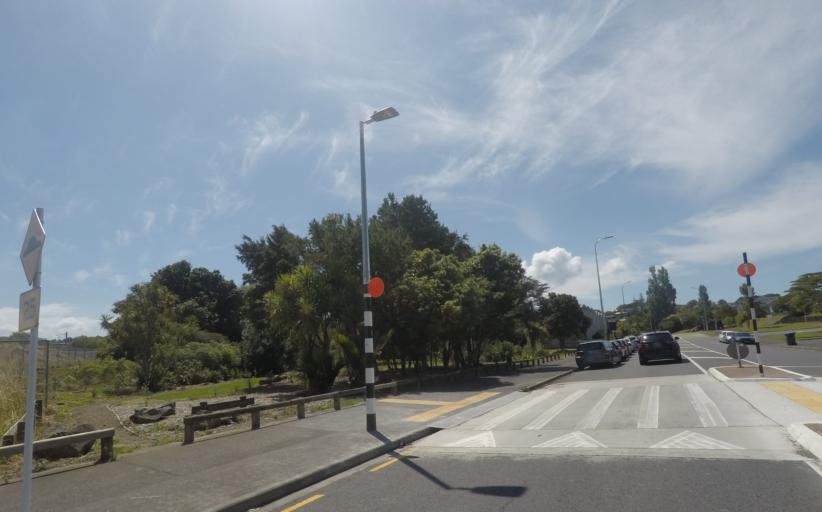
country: NZ
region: Auckland
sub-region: Auckland
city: Tamaki
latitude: -36.8731
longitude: 174.8532
